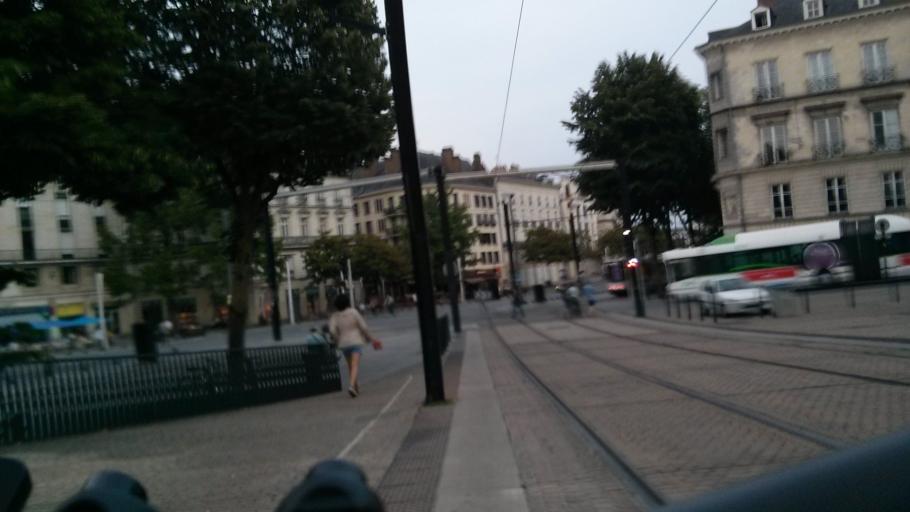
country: FR
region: Pays de la Loire
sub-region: Departement de la Loire-Atlantique
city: Nantes
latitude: 47.2166
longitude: -1.5573
